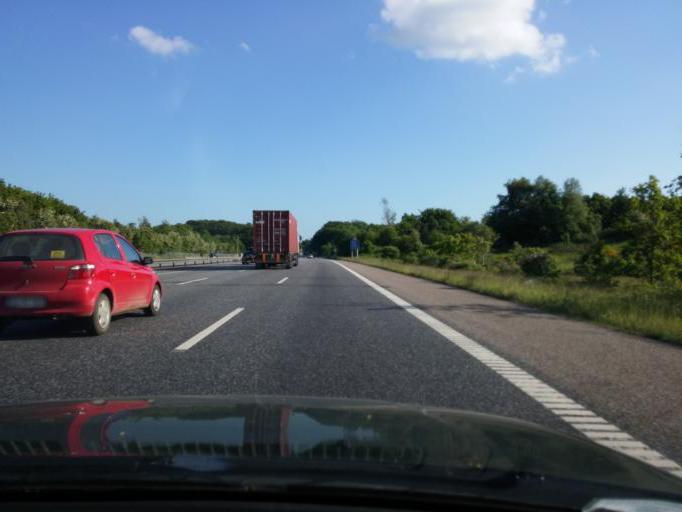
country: DK
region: South Denmark
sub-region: Kolding Kommune
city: Kolding
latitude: 55.4836
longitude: 9.4220
